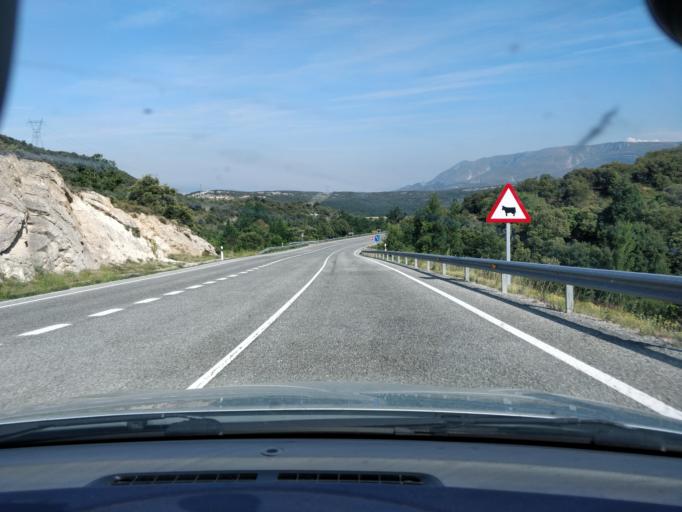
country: ES
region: Castille and Leon
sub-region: Provincia de Burgos
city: Medina de Pomar
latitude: 42.9112
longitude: -3.6048
